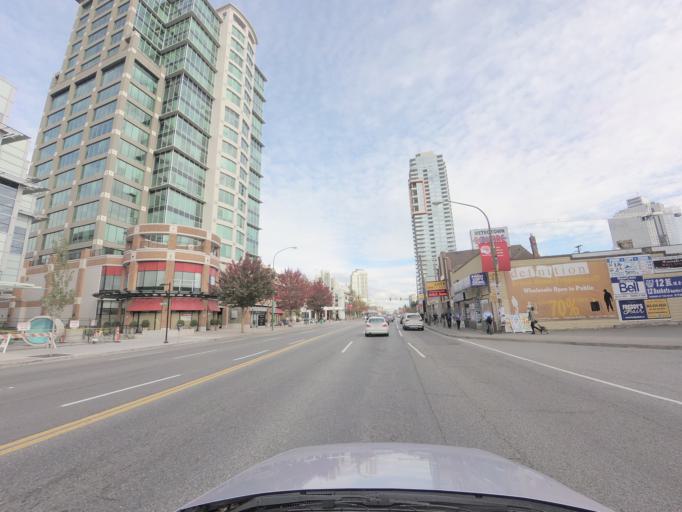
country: CA
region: British Columbia
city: Burnaby
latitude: 49.2298
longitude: -123.0037
